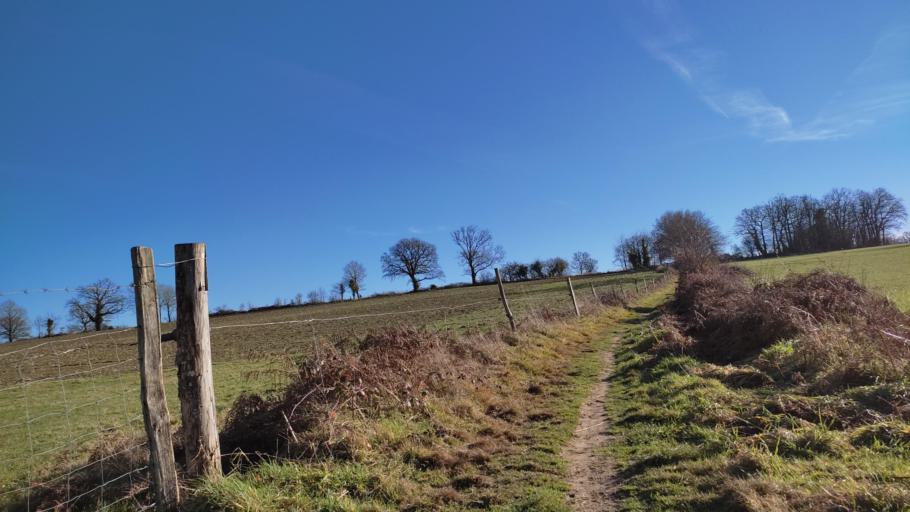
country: FR
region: Limousin
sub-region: Departement de la Haute-Vienne
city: Bosmie-l'Aiguille
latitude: 45.7523
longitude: 1.2123
